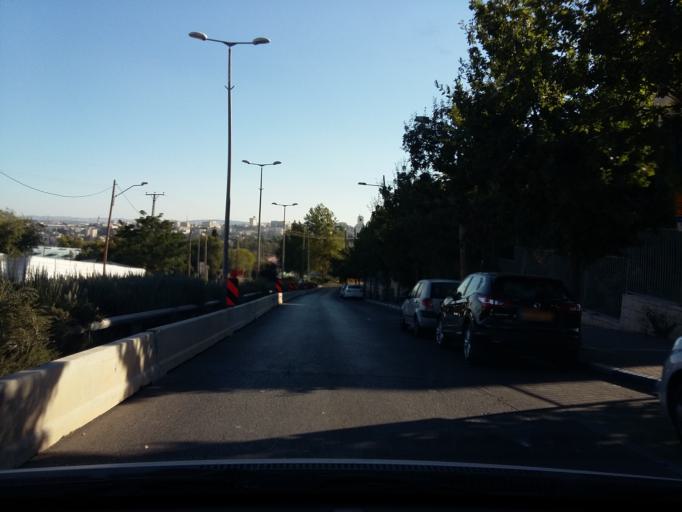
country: PS
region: West Bank
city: East Jerusalem
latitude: 31.7990
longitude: 35.2386
